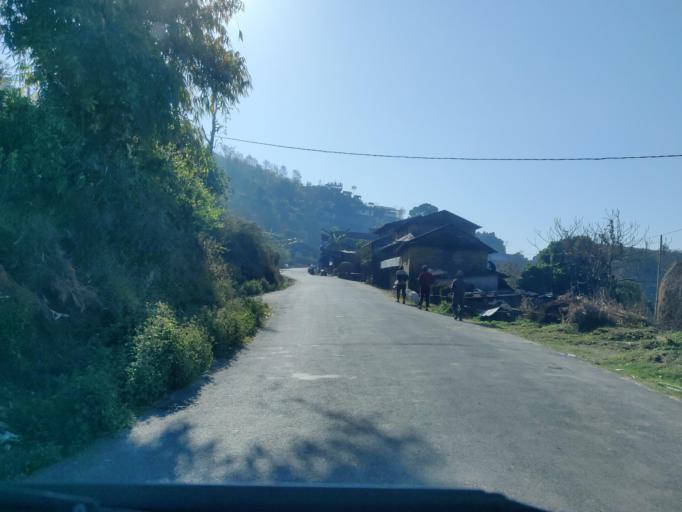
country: NP
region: Western Region
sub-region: Gandaki Zone
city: Pokhara
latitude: 28.2369
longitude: 83.9649
